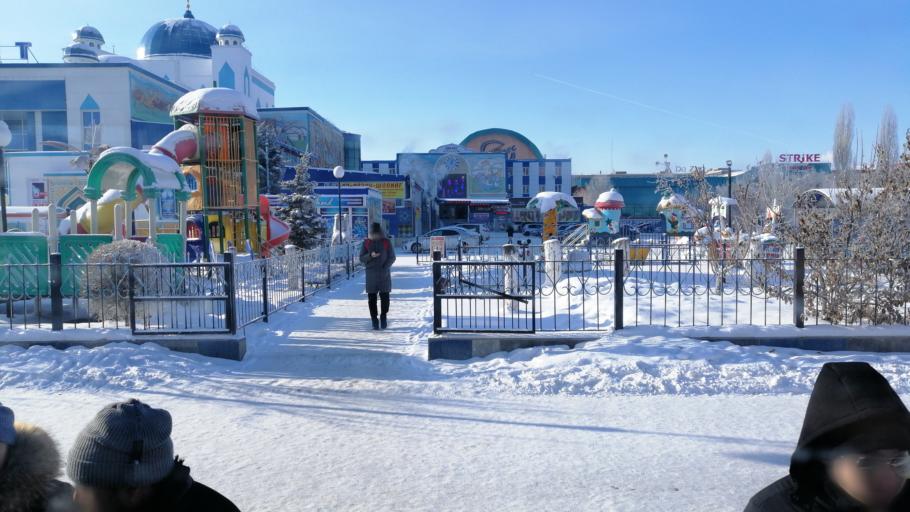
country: KZ
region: Aqtoebe
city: Aqtobe
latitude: 50.2970
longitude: 57.1568
